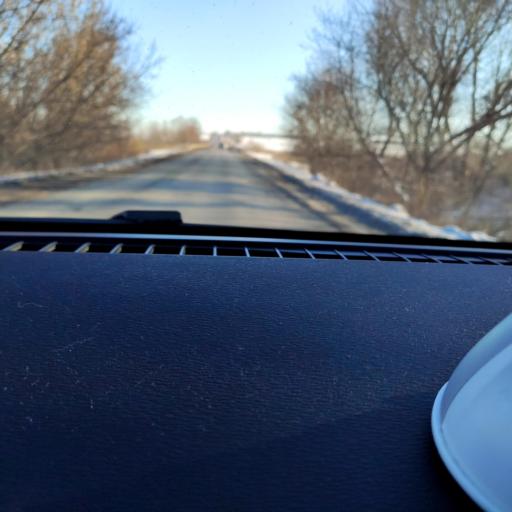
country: RU
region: Samara
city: Spiridonovka
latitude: 53.1445
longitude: 50.5520
